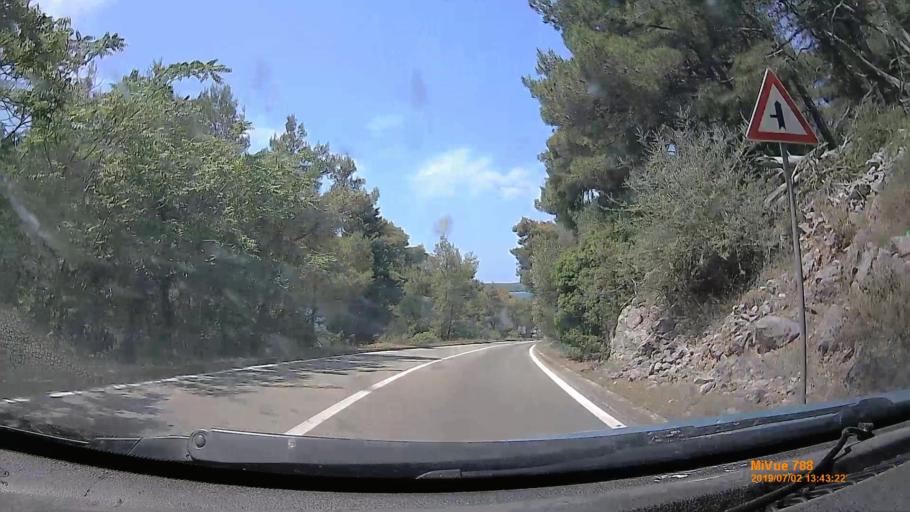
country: HR
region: Primorsko-Goranska
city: Mali Losinj
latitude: 44.5454
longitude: 14.4567
